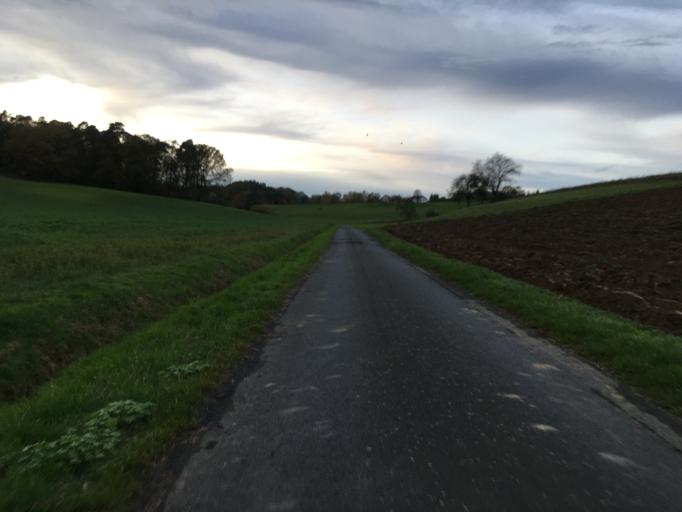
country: DE
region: Baden-Wuerttemberg
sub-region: Karlsruhe Region
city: Rosenberg
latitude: 49.3941
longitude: 9.4874
